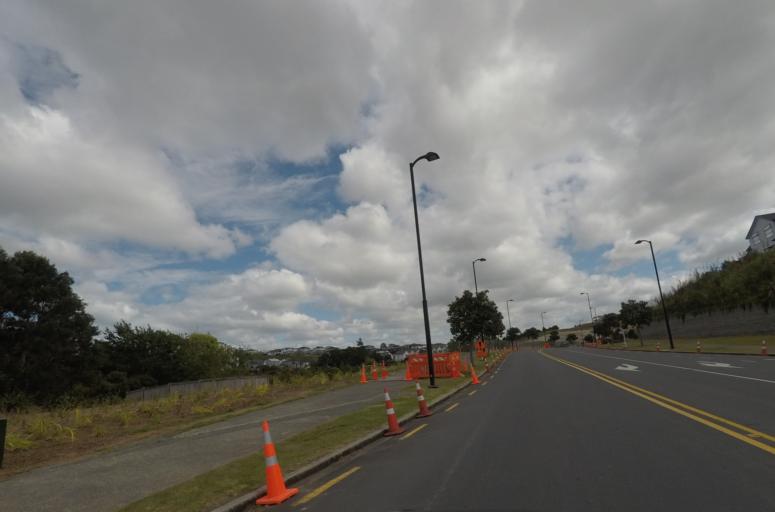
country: NZ
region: Auckland
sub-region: Auckland
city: Rothesay Bay
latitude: -36.5895
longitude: 174.6718
